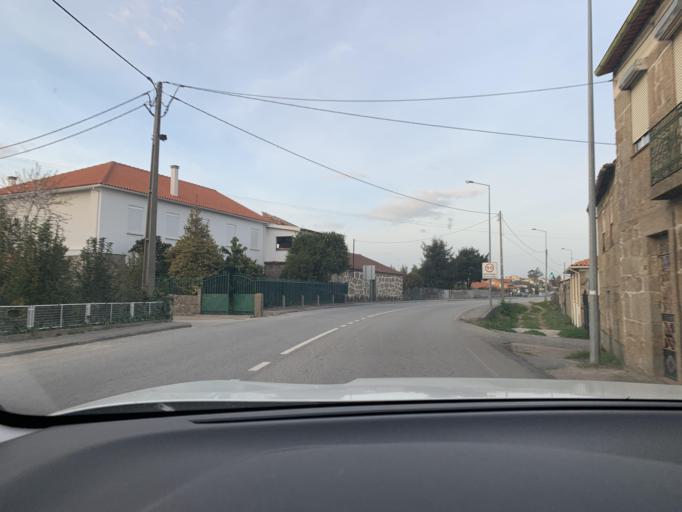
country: PT
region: Viseu
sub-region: Concelho de Tondela
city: Tondela
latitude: 40.4929
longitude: -8.0883
